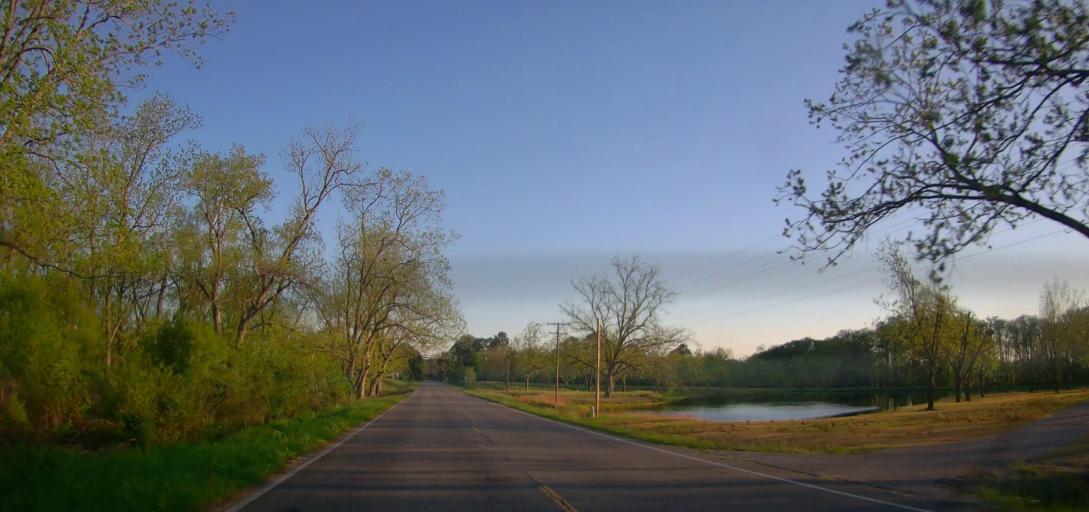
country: US
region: Georgia
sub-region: Irwin County
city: Ocilla
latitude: 31.6018
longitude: -83.2590
